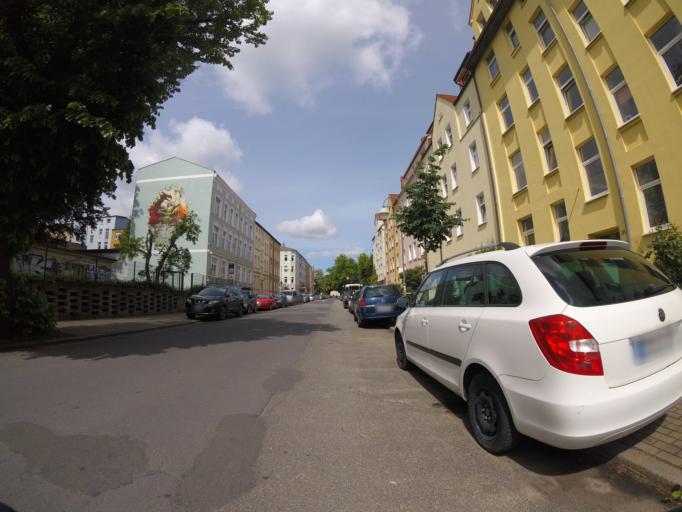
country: DE
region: Mecklenburg-Vorpommern
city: Rostock
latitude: 54.0892
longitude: 12.1091
